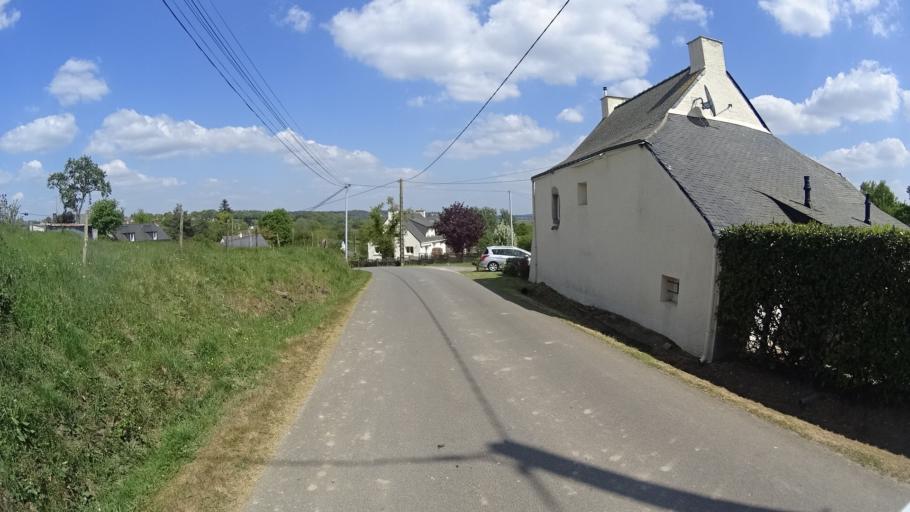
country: FR
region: Brittany
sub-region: Departement du Morbihan
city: Beganne
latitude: 47.5868
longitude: -2.2422
